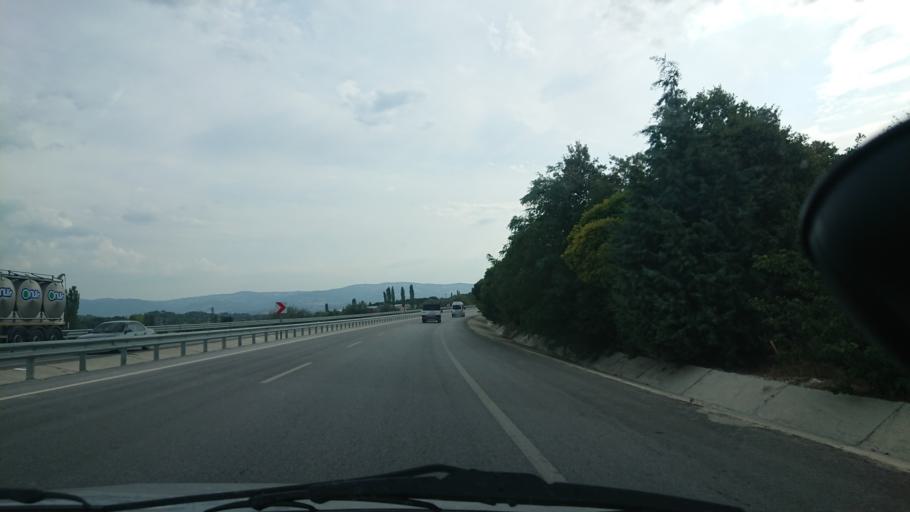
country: TR
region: Kuetahya
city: Gediz
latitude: 39.0185
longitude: 29.4130
